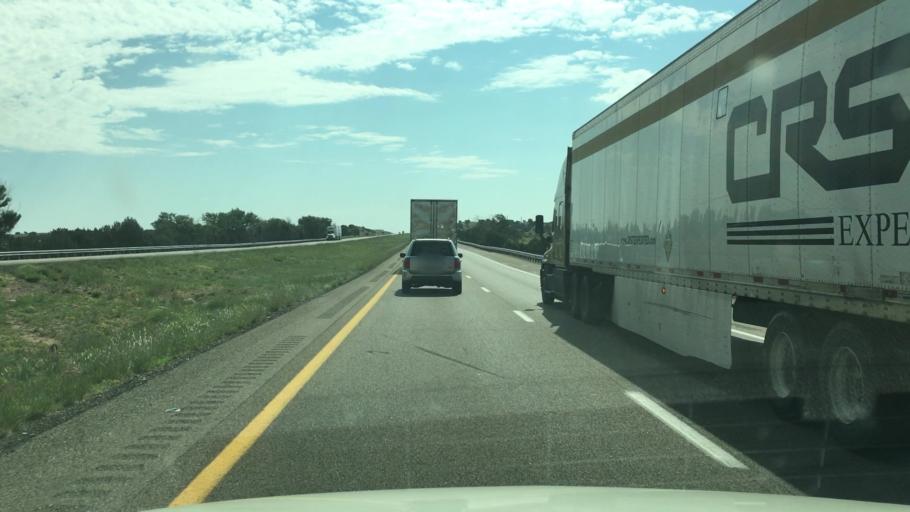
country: US
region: New Mexico
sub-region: Guadalupe County
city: Santa Rosa
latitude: 34.9749
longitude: -104.9624
